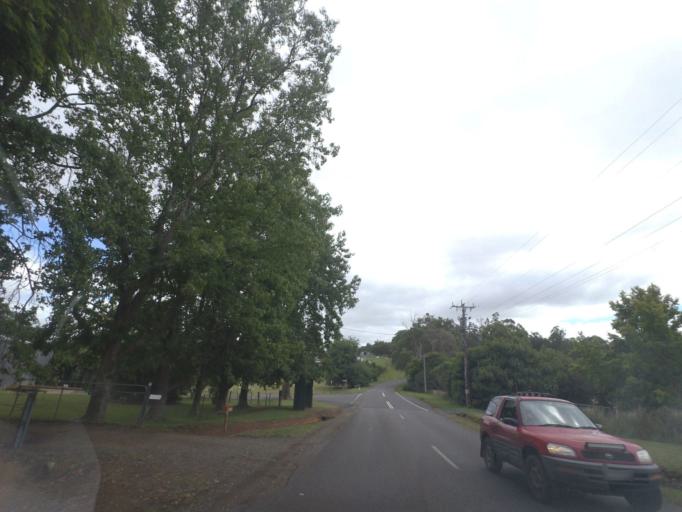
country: AU
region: Victoria
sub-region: Yarra Ranges
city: Launching Place
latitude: -37.8354
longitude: 145.5843
